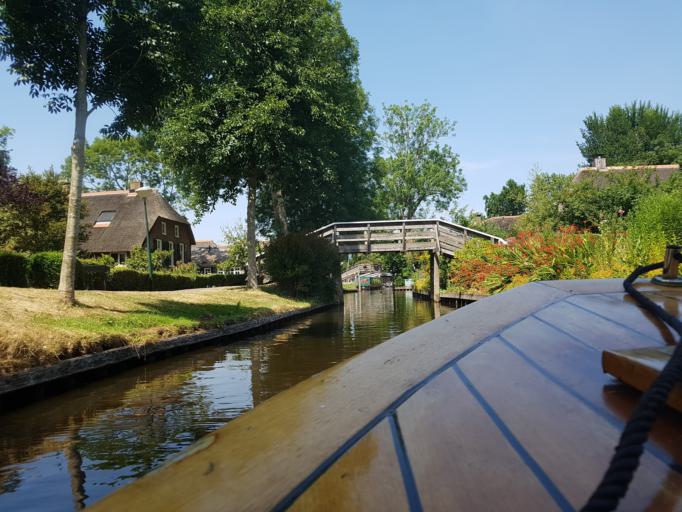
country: NL
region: Overijssel
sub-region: Gemeente Steenwijkerland
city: Giethoorn
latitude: 52.7198
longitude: 6.0904
